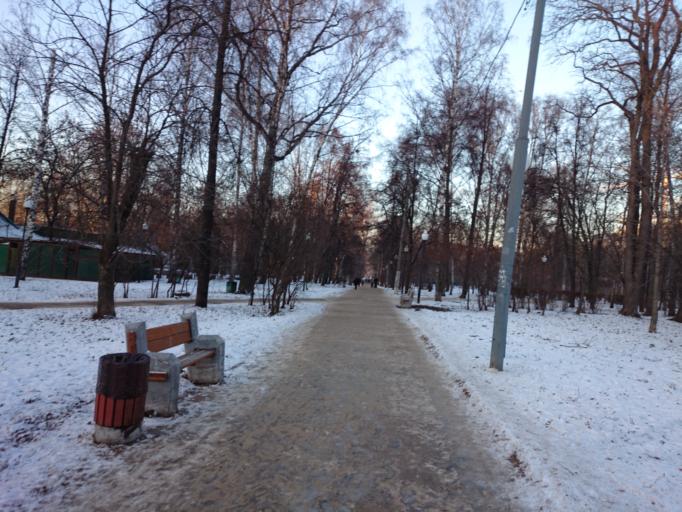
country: RU
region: Moscow
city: Sokol
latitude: 55.7885
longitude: 37.5135
